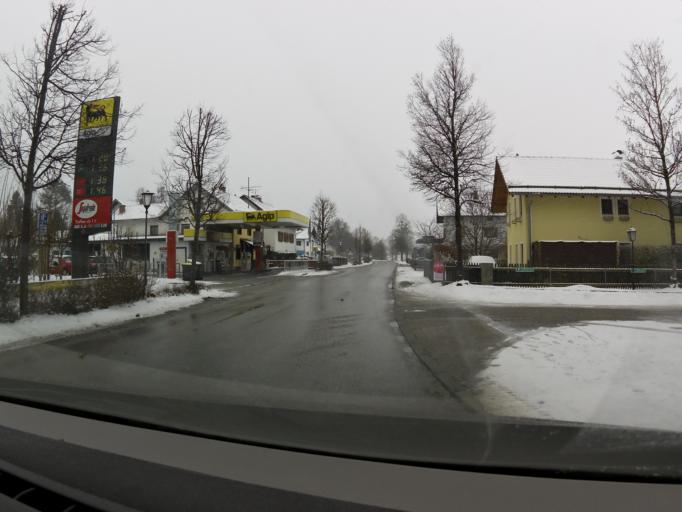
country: DE
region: Bavaria
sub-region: Upper Bavaria
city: Bichl
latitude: 47.7185
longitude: 11.4131
